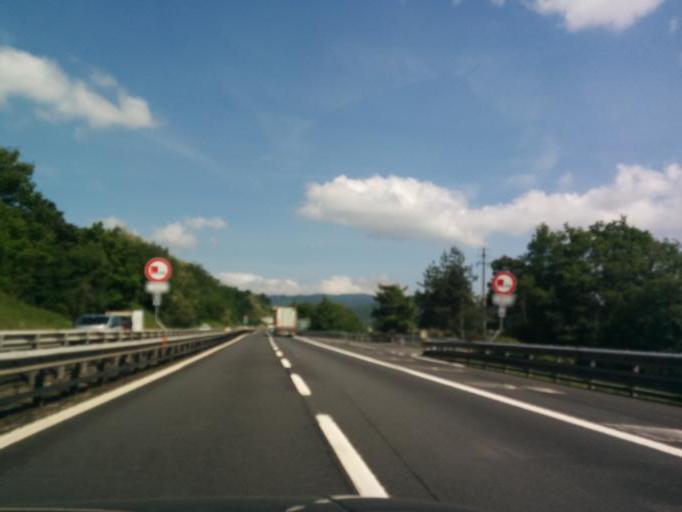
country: IT
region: Tuscany
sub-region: Province of Florence
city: Barberino di Mugello
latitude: 44.0201
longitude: 11.2242
